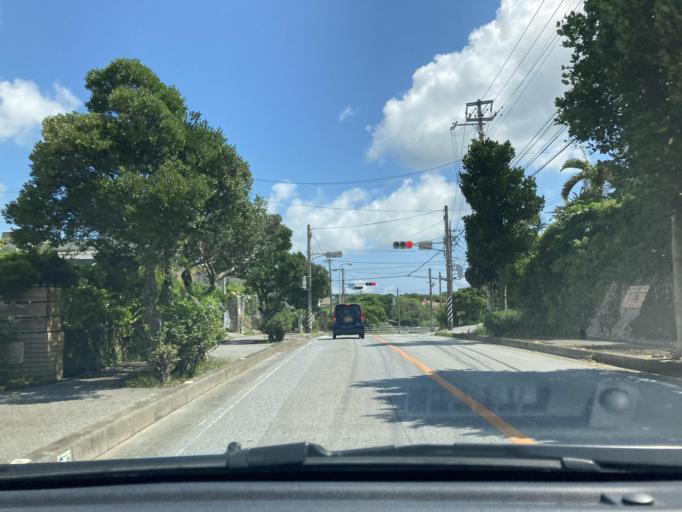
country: JP
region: Okinawa
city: Tomigusuku
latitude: 26.1530
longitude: 127.7749
